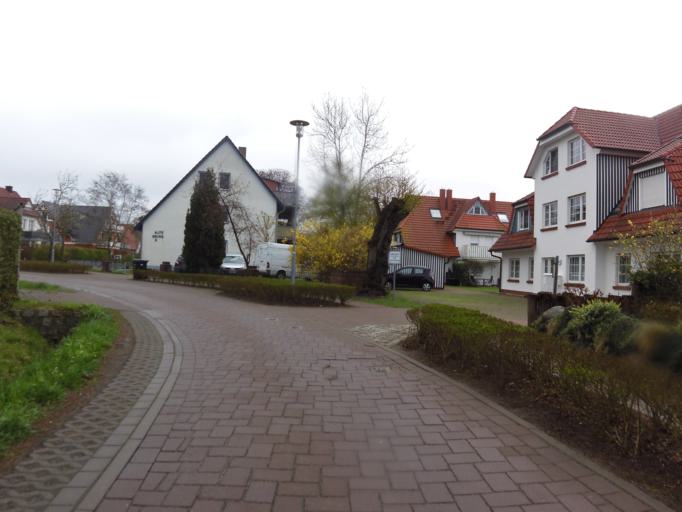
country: DE
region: Mecklenburg-Vorpommern
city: Zingst
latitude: 54.4372
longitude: 12.6799
